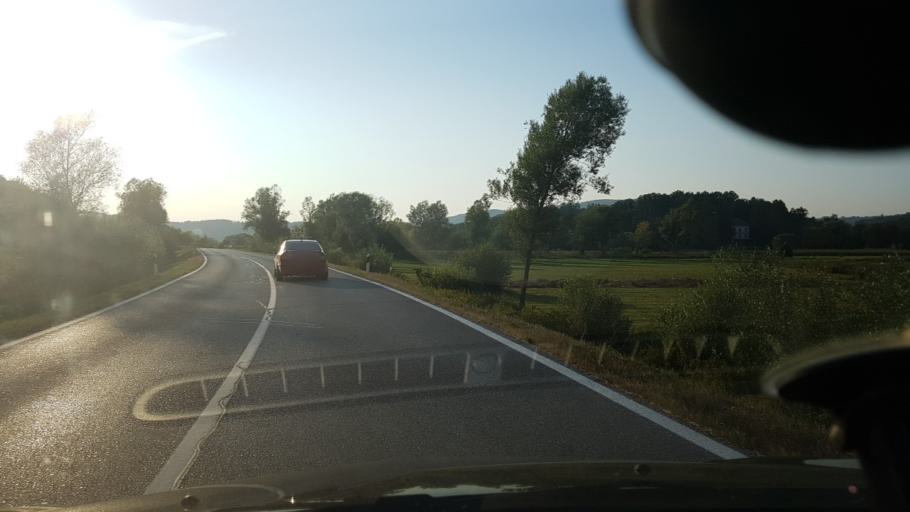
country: HR
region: Krapinsko-Zagorska
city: Pregrada
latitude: 46.1411
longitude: 15.7880
